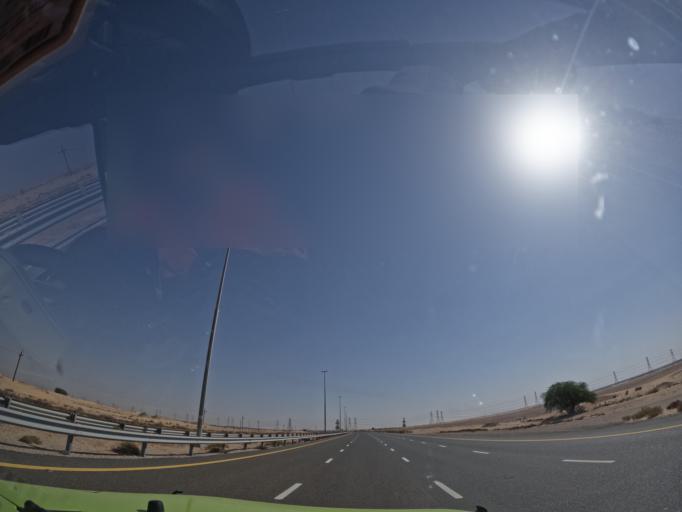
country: AE
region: Ash Shariqah
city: Sharjah
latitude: 25.0135
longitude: 55.5352
